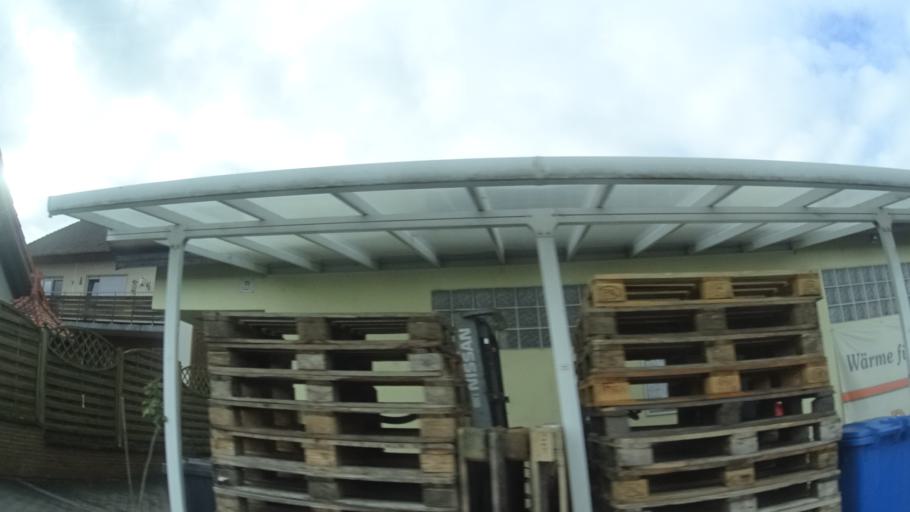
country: DE
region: Bavaria
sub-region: Regierungsbezirk Unterfranken
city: Hochheim
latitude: 50.3663
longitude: 10.4702
